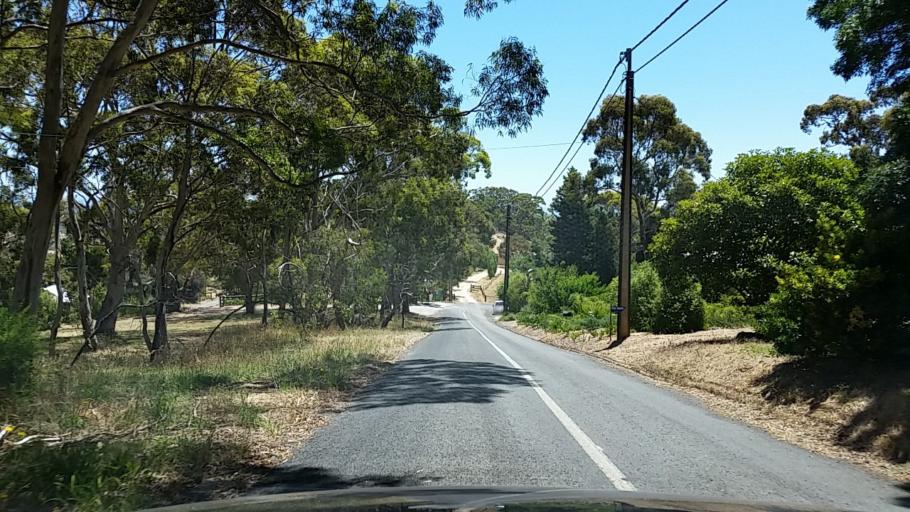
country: AU
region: South Australia
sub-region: Adelaide Hills
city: Upper Sturt
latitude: -34.9899
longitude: 138.6724
